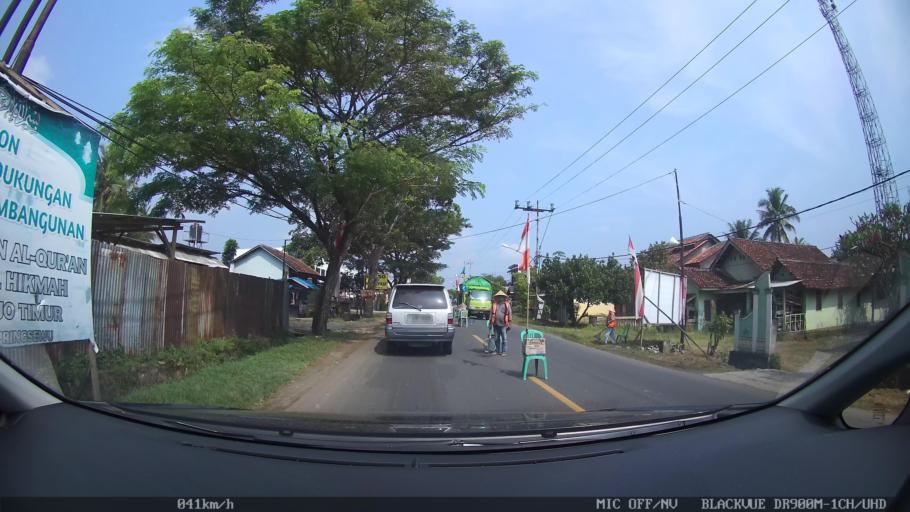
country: ID
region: Lampung
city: Gadingrejo
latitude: -5.3730
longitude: 105.0788
